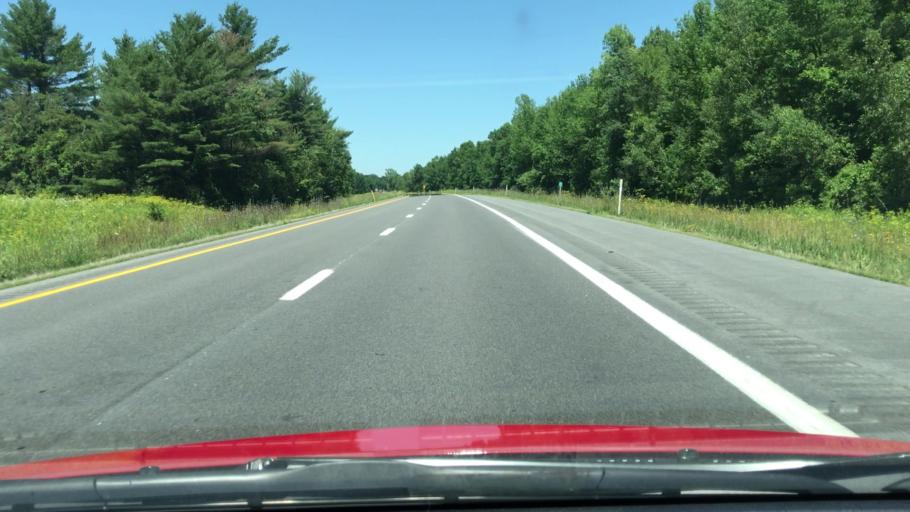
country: US
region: New York
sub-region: Clinton County
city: Cumberland Head
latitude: 44.8432
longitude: -73.4465
